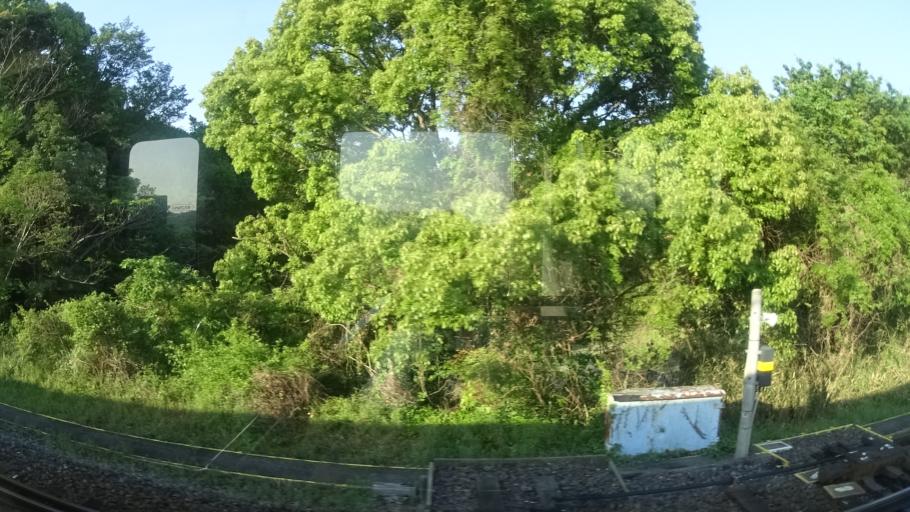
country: JP
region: Mie
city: Ise
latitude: 34.4773
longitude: 136.7255
